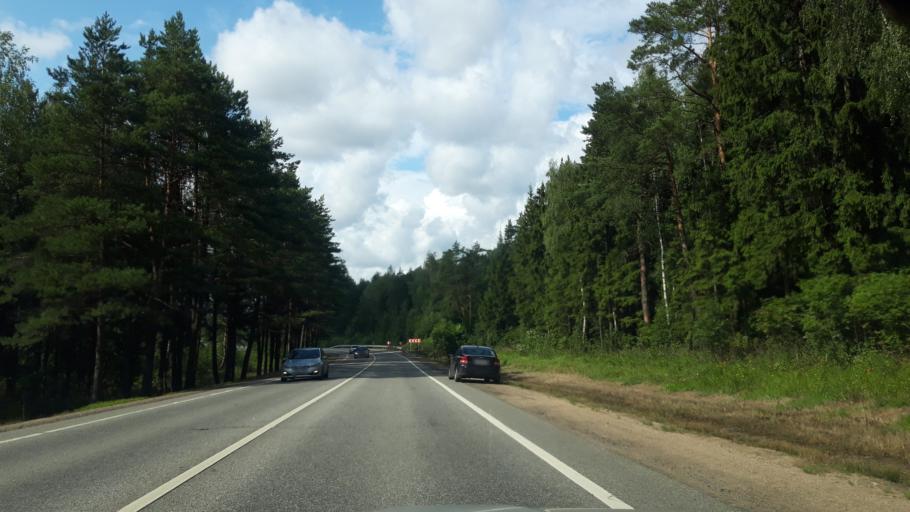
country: RU
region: Moskovskaya
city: Andreyevka
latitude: 55.9502
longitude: 37.1260
